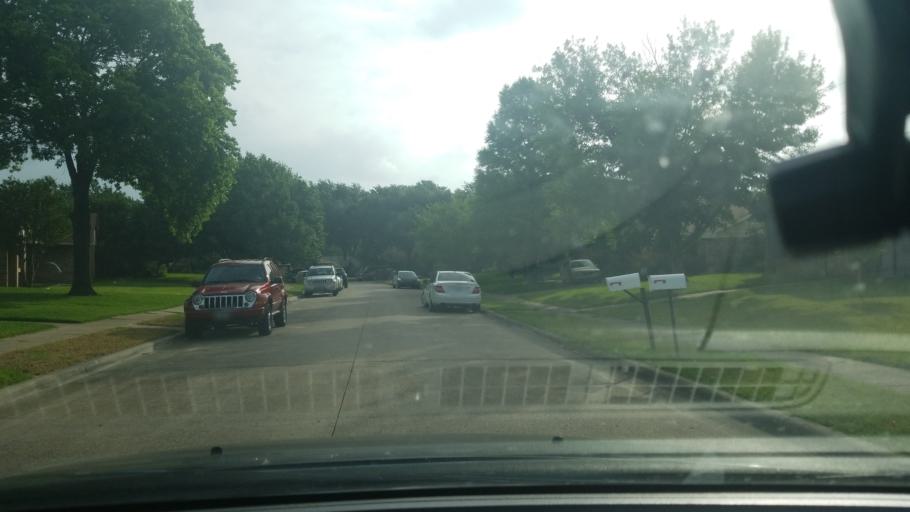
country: US
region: Texas
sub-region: Dallas County
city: Mesquite
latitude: 32.7875
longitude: -96.6456
